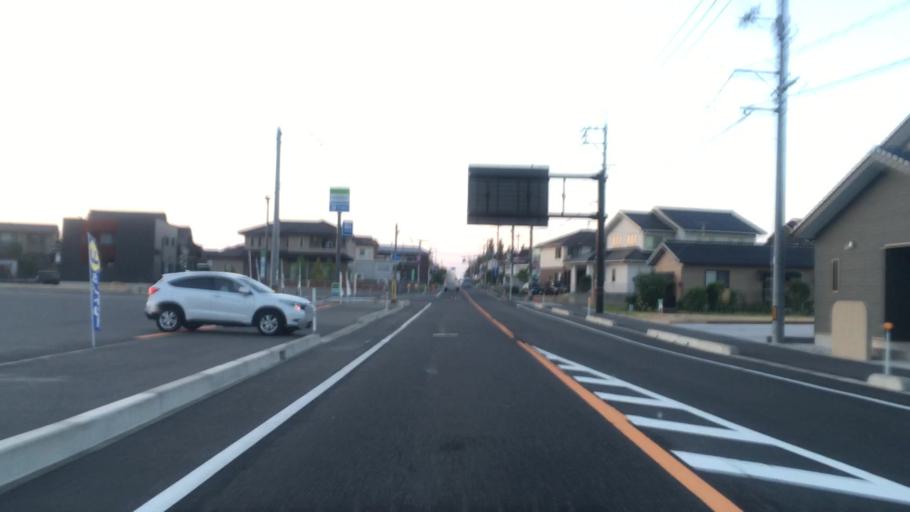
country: JP
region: Tottori
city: Tottori
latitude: 35.5830
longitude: 134.3326
